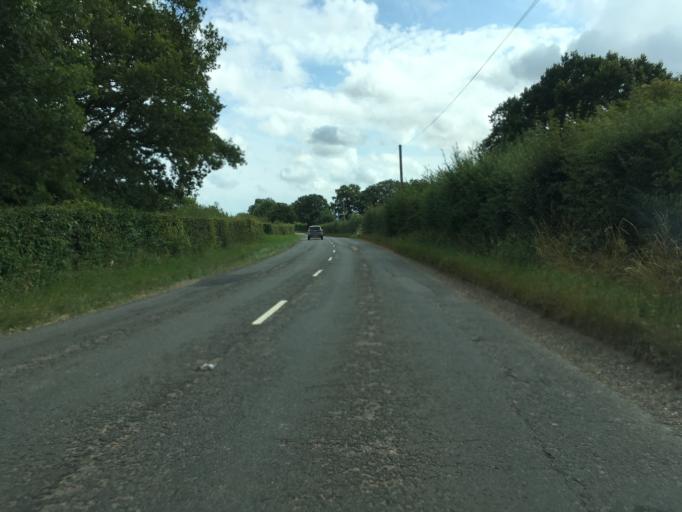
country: GB
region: England
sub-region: Kent
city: Tenterden
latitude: 51.0543
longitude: 0.7309
